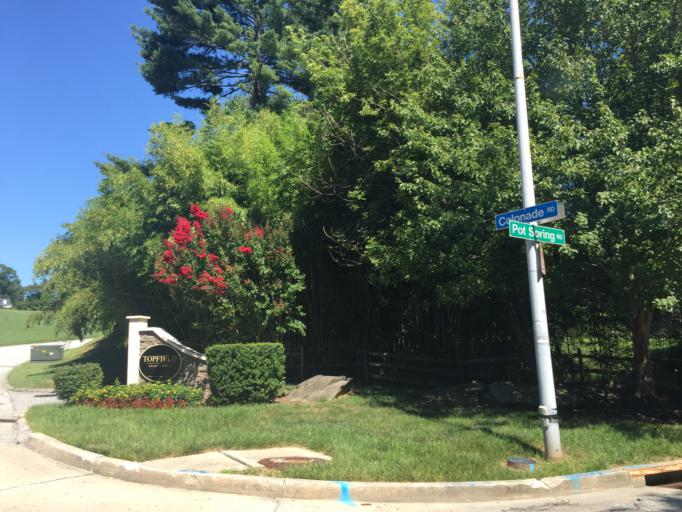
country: US
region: Maryland
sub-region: Baltimore County
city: Timonium
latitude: 39.4750
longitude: -76.5974
